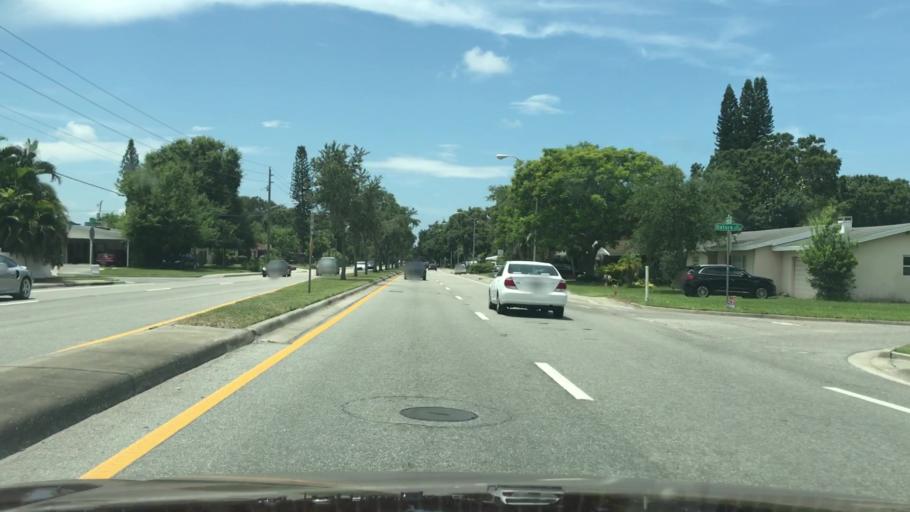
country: US
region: Florida
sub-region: Sarasota County
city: Southgate
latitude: 27.3149
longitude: -82.5142
